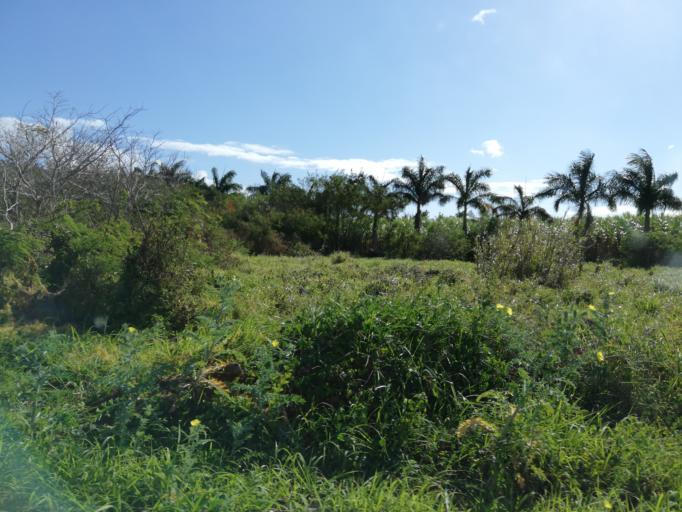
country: MU
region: Riviere du Rempart
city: Petit Raffray
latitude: -20.0164
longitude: 57.6001
